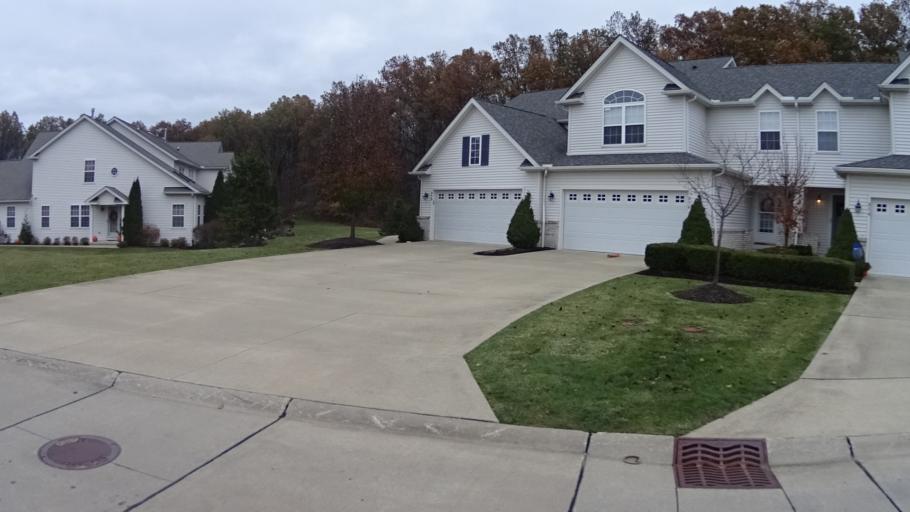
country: US
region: Ohio
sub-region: Lorain County
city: Avon Center
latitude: 41.4803
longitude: -82.0152
